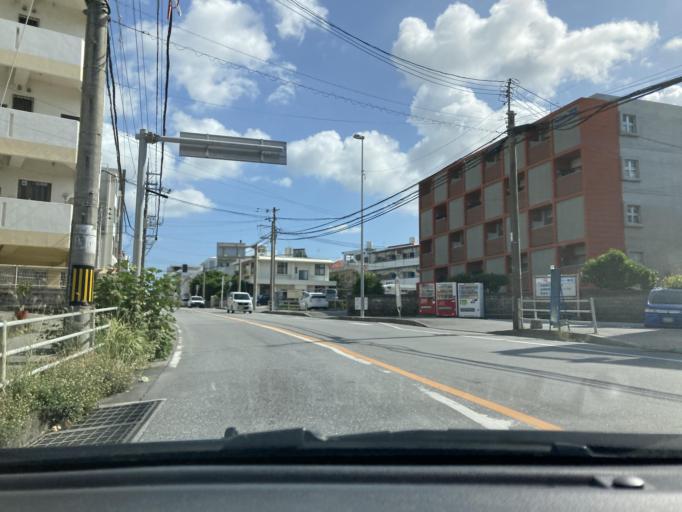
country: JP
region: Okinawa
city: Tomigusuku
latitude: 26.1873
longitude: 127.6802
